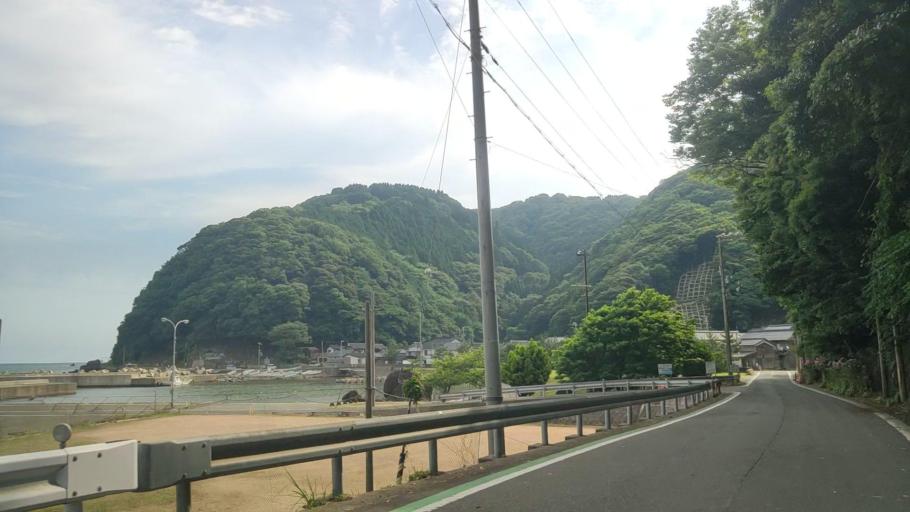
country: JP
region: Hyogo
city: Toyooka
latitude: 35.6432
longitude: 134.8429
